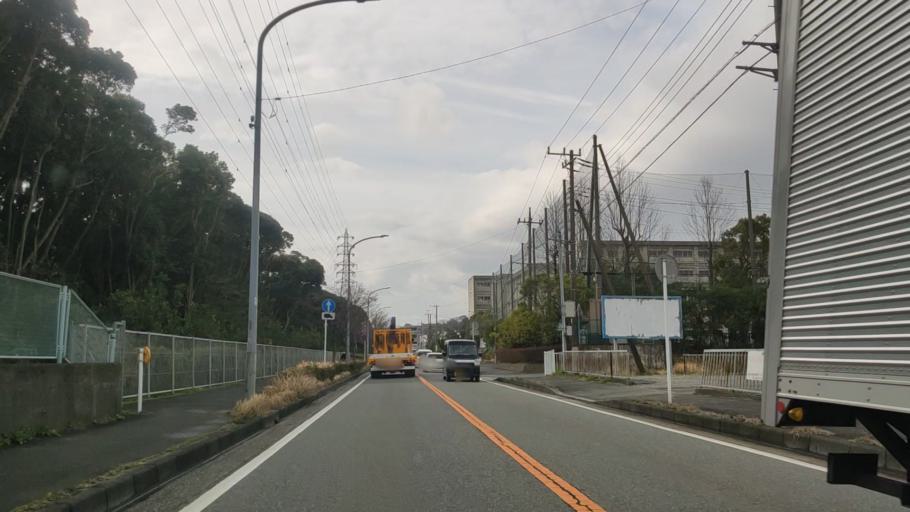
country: JP
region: Kanagawa
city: Fujisawa
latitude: 35.3755
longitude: 139.5248
